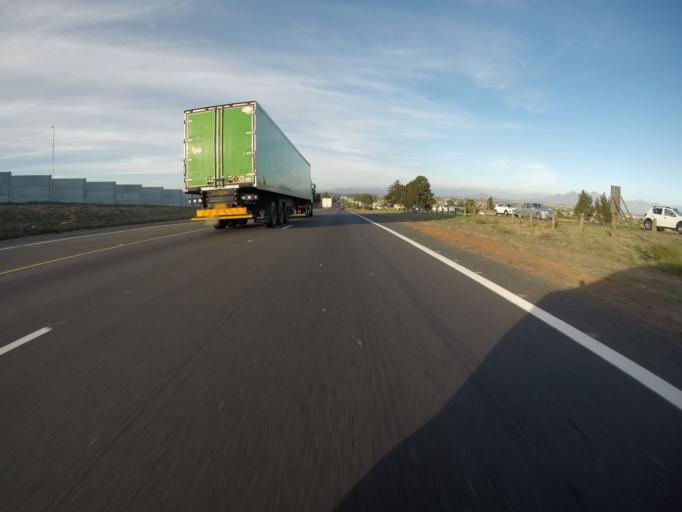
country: ZA
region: Western Cape
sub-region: City of Cape Town
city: Kraaifontein
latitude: -33.8560
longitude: 18.6983
